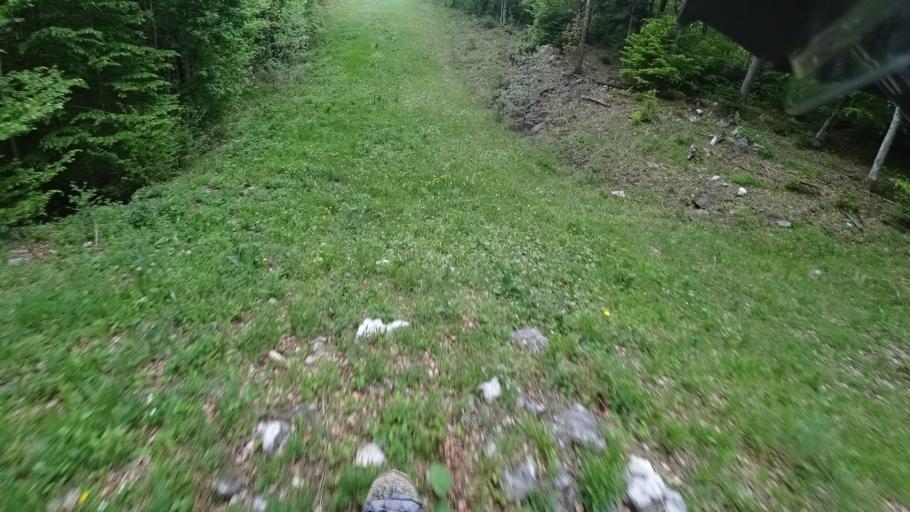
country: HR
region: Licko-Senjska
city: Otocac
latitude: 44.9016
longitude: 15.4130
